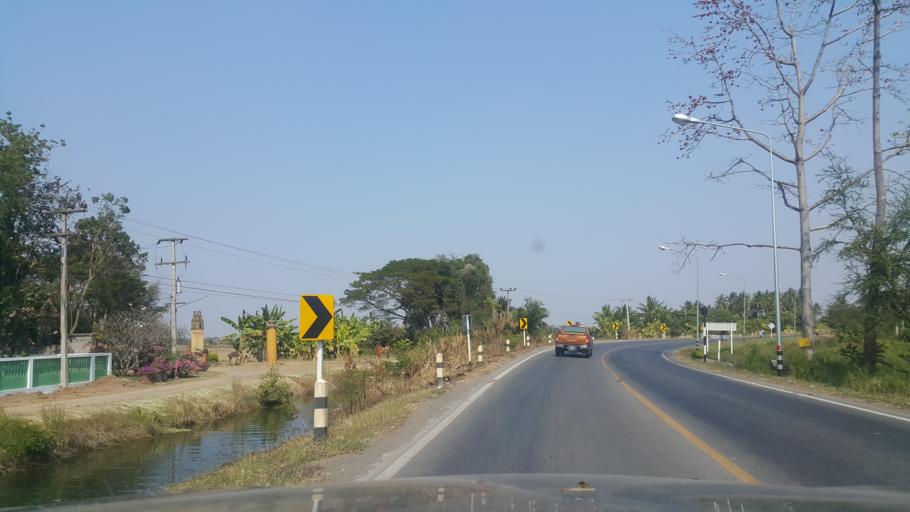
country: TH
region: Nakhon Ratchasima
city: Pak Thong Chai
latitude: 14.6950
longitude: 102.0273
